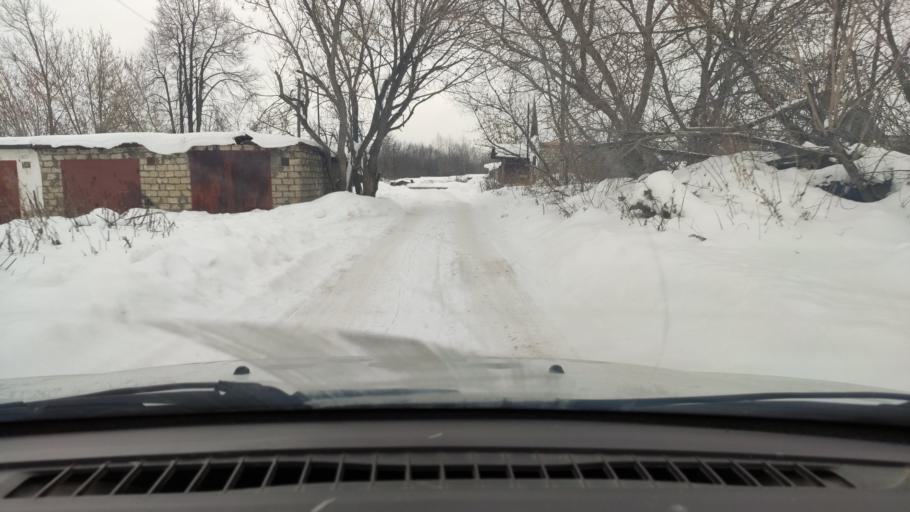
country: RU
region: Perm
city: Kungur
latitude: 57.4494
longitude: 56.9308
